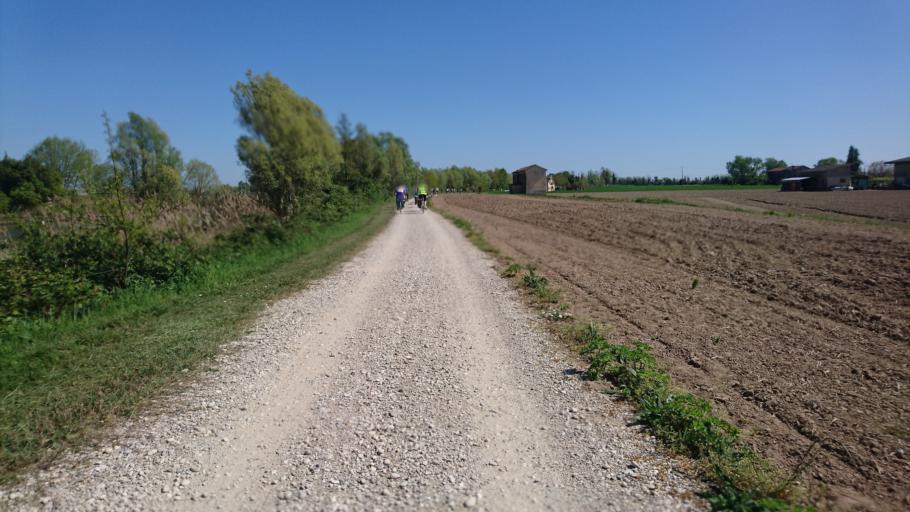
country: IT
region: Veneto
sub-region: Provincia di Venezia
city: Passarella
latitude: 45.5548
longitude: 12.5756
